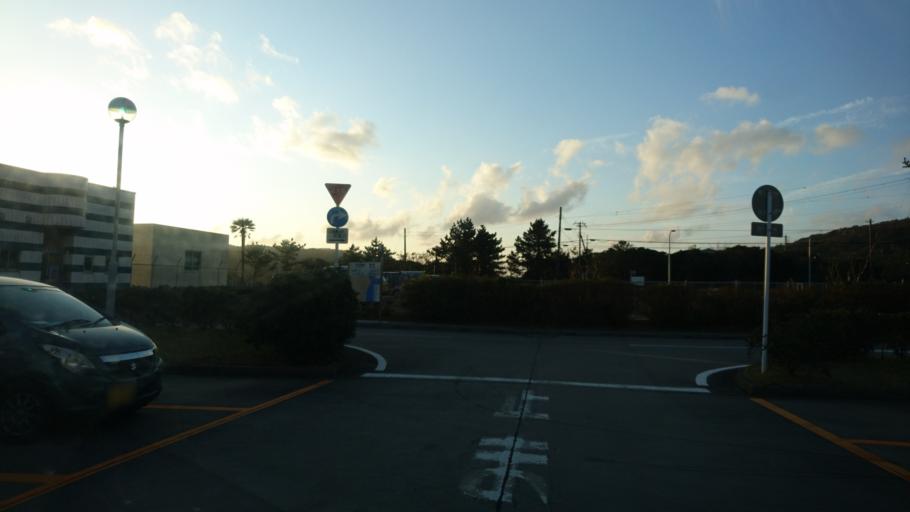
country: JP
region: Shizuoka
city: Shimoda
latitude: 34.3707
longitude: 139.2693
